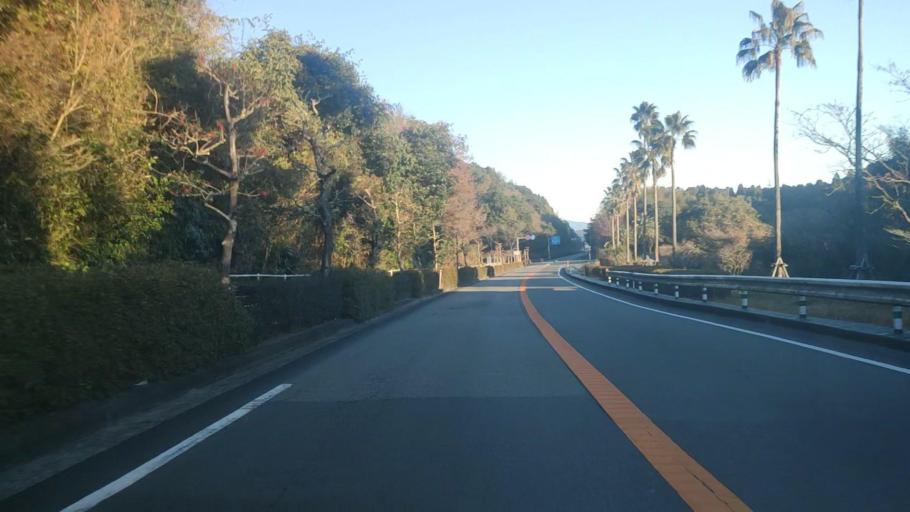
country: JP
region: Miyazaki
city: Tsuma
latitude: 32.0277
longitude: 131.4641
